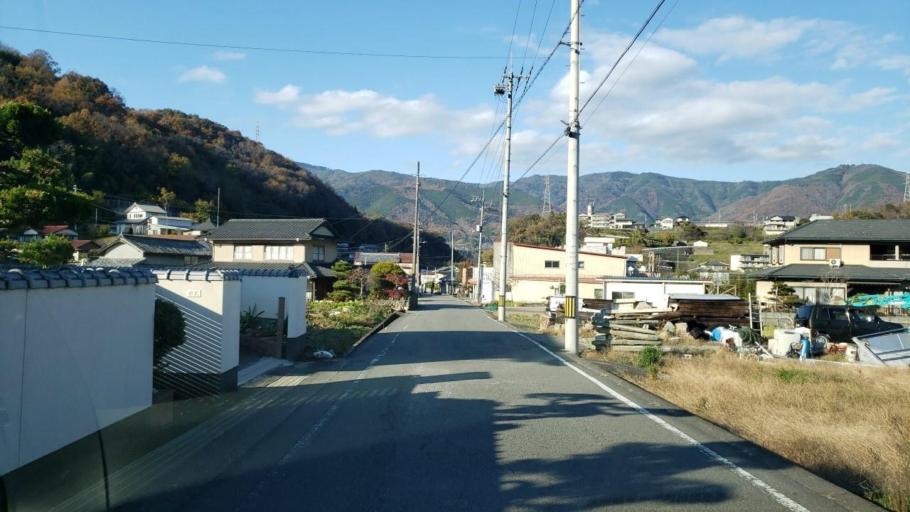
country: JP
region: Tokushima
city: Wakimachi
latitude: 34.0344
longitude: 134.0289
